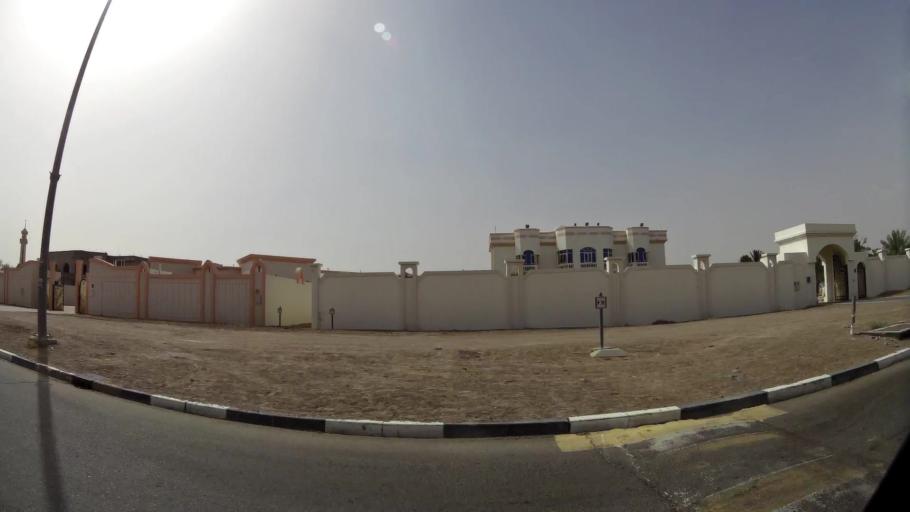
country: AE
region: Abu Dhabi
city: Al Ain
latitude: 24.1865
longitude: 55.6128
